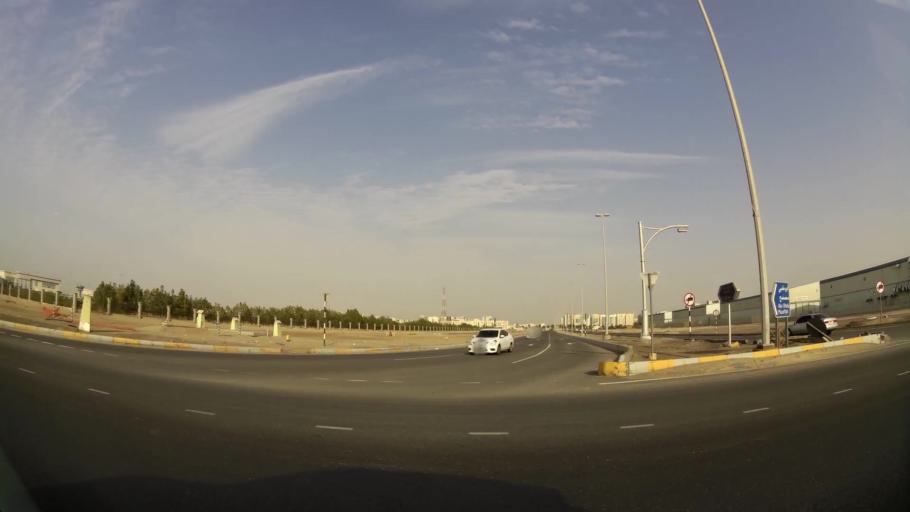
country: AE
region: Abu Dhabi
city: Abu Dhabi
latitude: 24.3387
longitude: 54.5175
